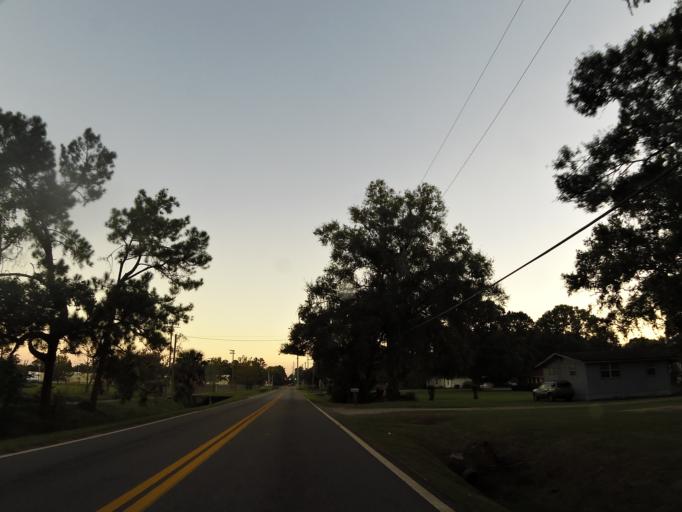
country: US
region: Florida
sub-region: Duval County
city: Jacksonville
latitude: 30.3124
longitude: -81.7436
